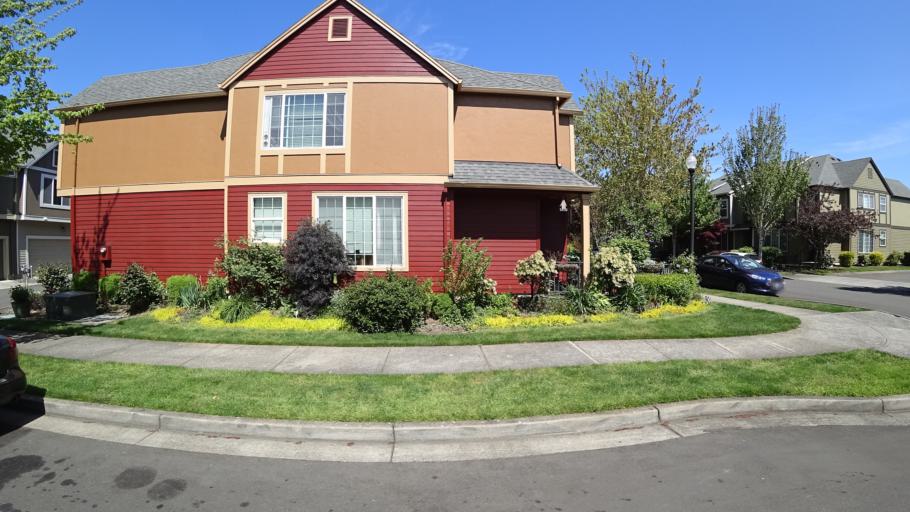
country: US
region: Oregon
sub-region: Washington County
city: Hillsboro
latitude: 45.5086
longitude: -122.9711
